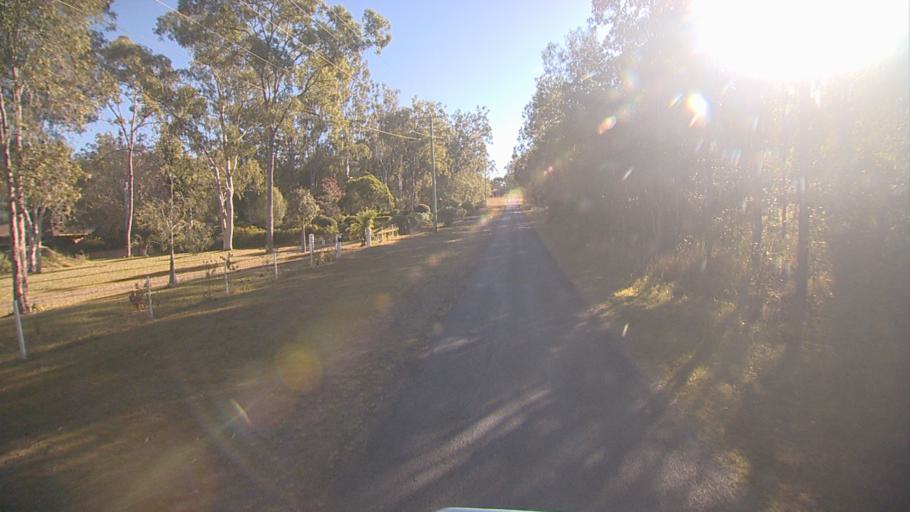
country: AU
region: Queensland
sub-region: Logan
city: North Maclean
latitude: -27.7889
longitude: 152.9609
